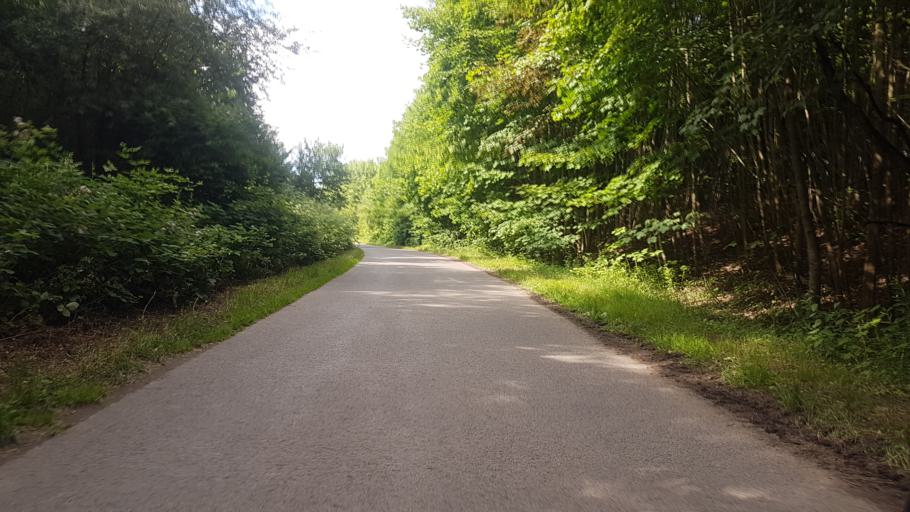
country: DE
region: Saarland
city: Saarlouis
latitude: 49.3023
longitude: 6.7645
